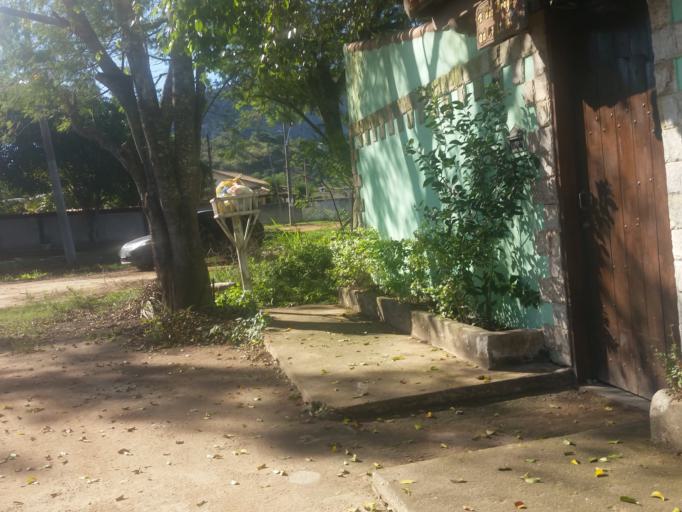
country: BR
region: Rio de Janeiro
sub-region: Marica
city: Marica
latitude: -22.9553
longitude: -42.9664
